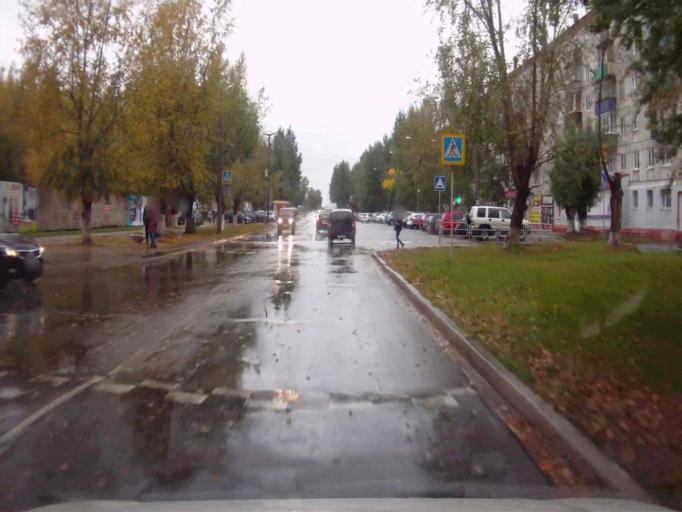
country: RU
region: Chelyabinsk
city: Kyshtym
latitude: 55.7016
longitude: 60.5558
